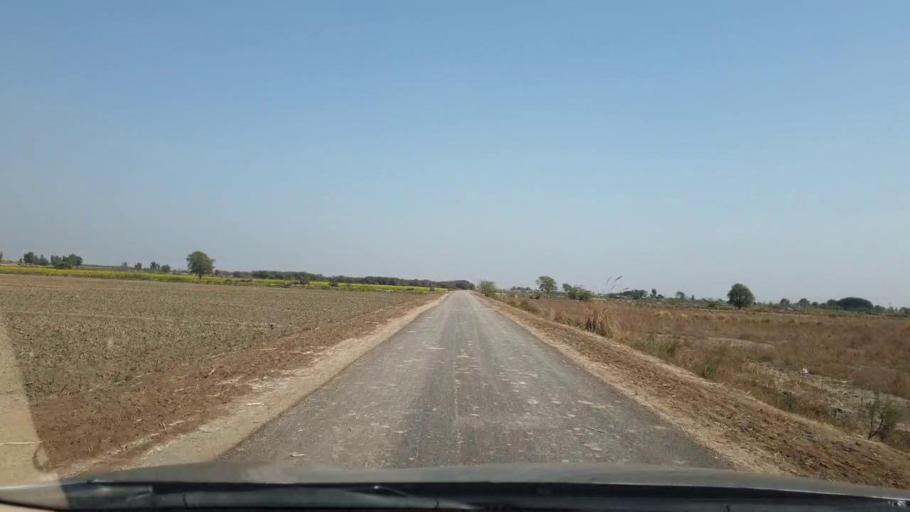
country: PK
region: Sindh
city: Mirpur Khas
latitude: 25.5670
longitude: 68.8861
